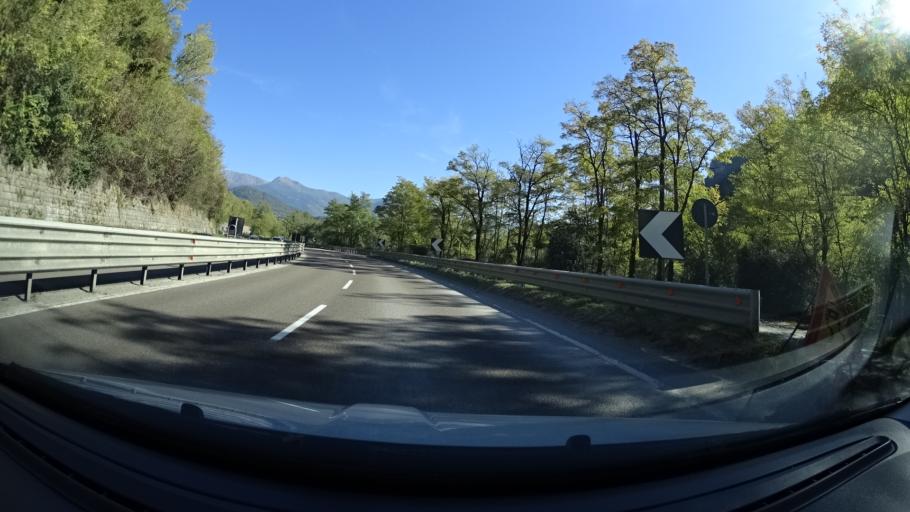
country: IT
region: Trentino-Alto Adige
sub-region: Provincia di Trento
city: Civezzano
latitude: 46.0825
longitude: 11.1856
